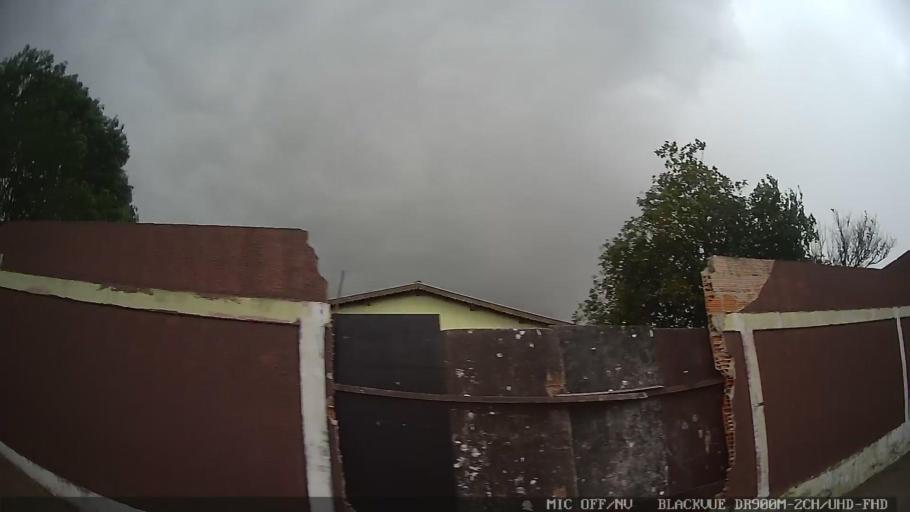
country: BR
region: Sao Paulo
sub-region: Indaiatuba
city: Indaiatuba
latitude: -23.1330
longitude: -47.2422
